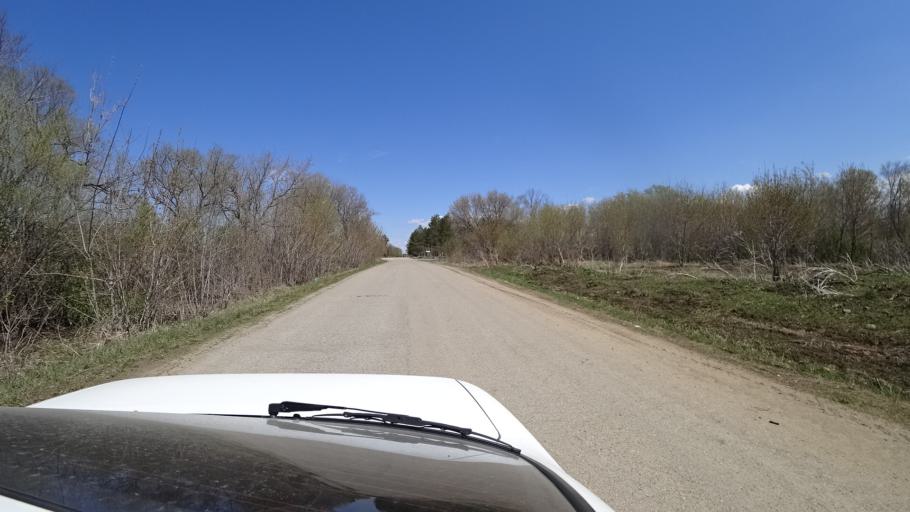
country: RU
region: Primorskiy
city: Lazo
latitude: 45.7960
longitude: 133.7640
